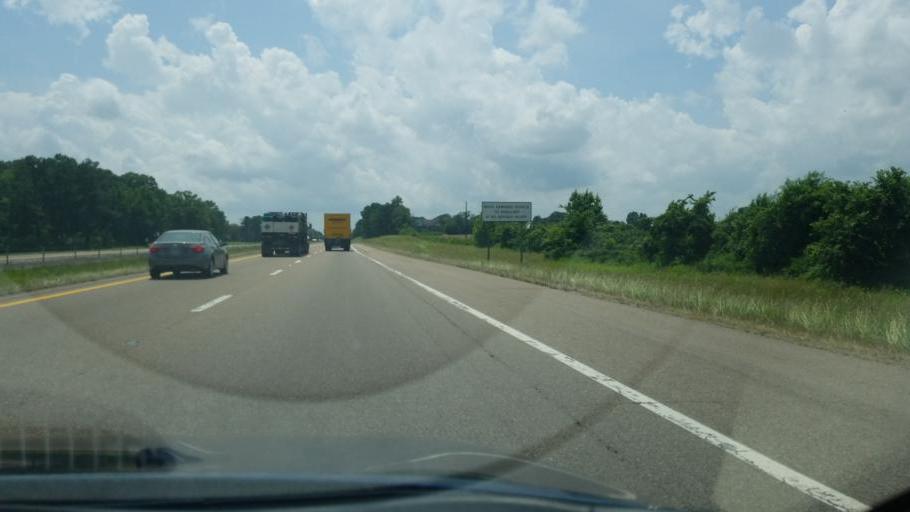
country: US
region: Tennessee
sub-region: Crockett County
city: Bells
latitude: 35.6258
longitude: -88.9732
